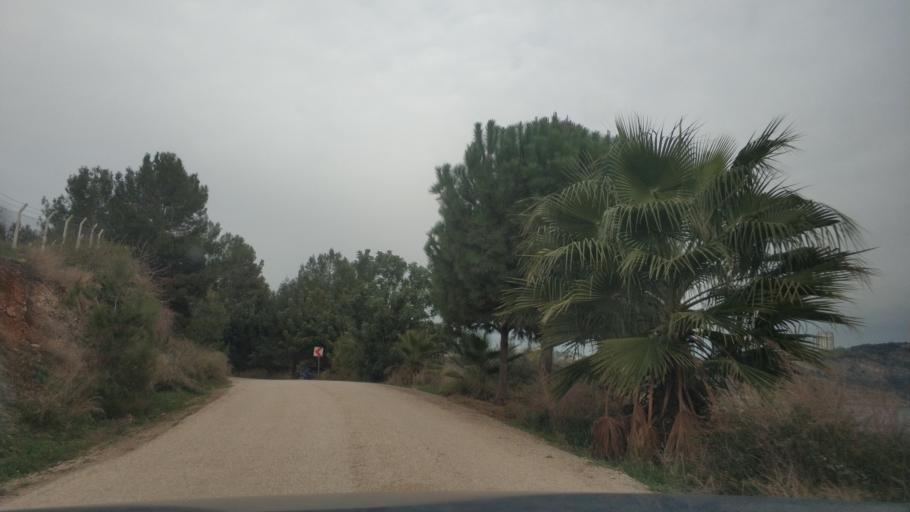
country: TR
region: Adana
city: Adana
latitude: 37.0764
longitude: 35.3249
